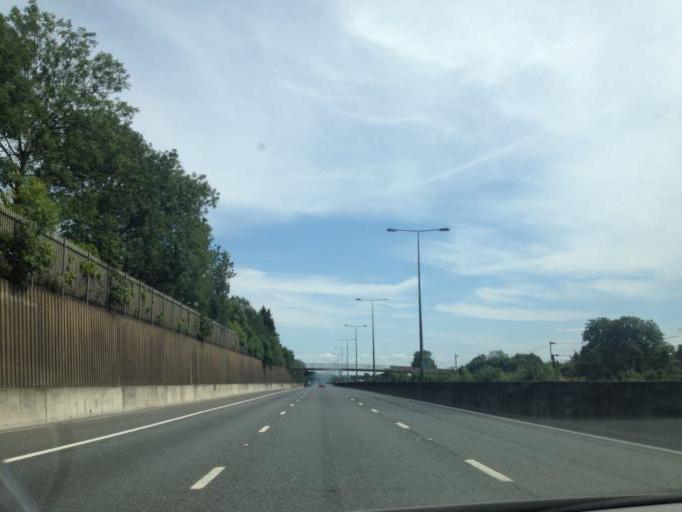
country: GB
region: England
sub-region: Greater London
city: Edgware
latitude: 51.6197
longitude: -0.2552
